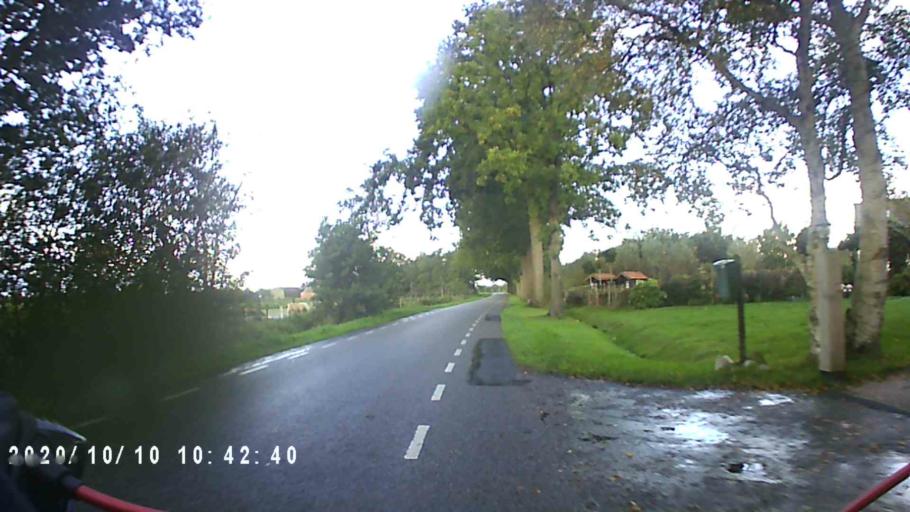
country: NL
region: Groningen
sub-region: Gemeente Grootegast
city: Grootegast
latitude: 53.1735
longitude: 6.2724
